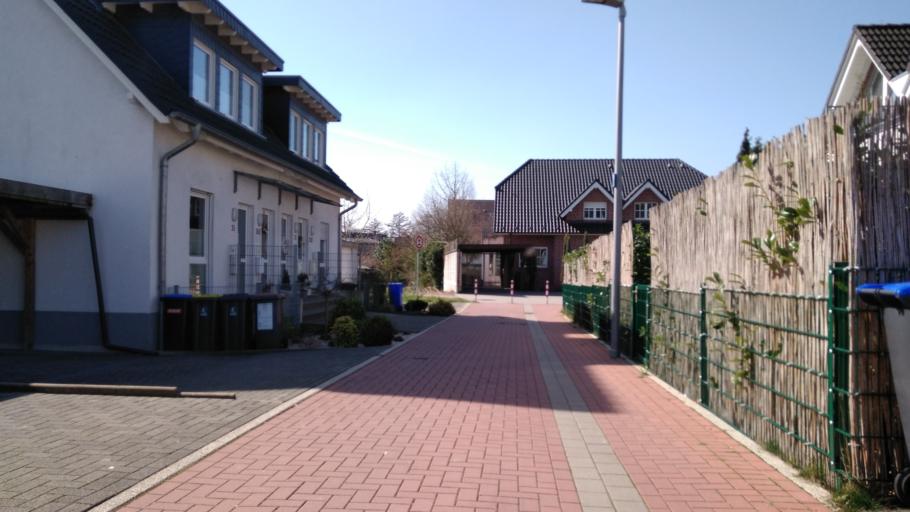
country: DE
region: North Rhine-Westphalia
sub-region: Regierungsbezirk Munster
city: Gladbeck
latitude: 51.5962
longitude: 6.9299
